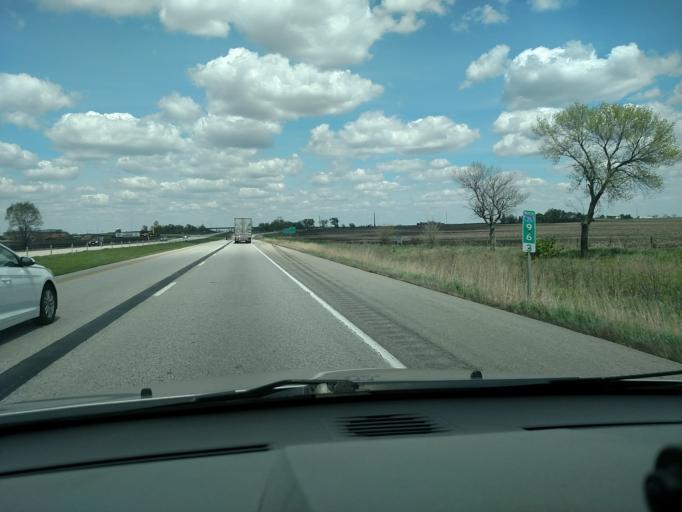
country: US
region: Iowa
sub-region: Polk County
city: Ankeny
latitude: 41.7840
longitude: -93.5704
